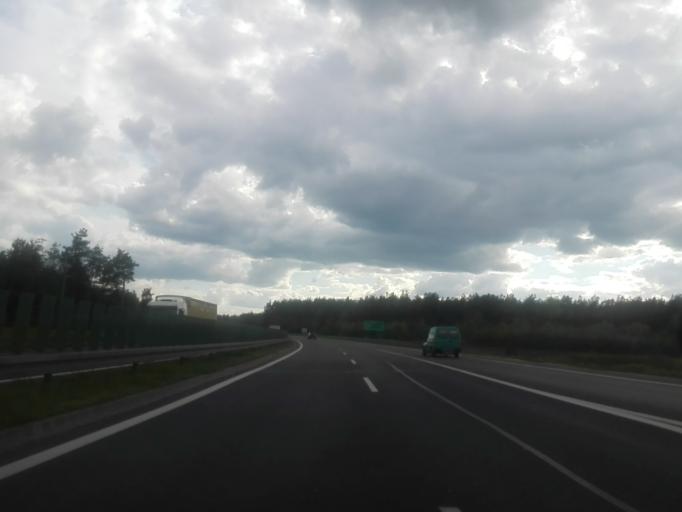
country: PL
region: Masovian Voivodeship
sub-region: Powiat ostrowski
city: Ostrow Mazowiecka
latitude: 52.8173
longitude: 21.8837
